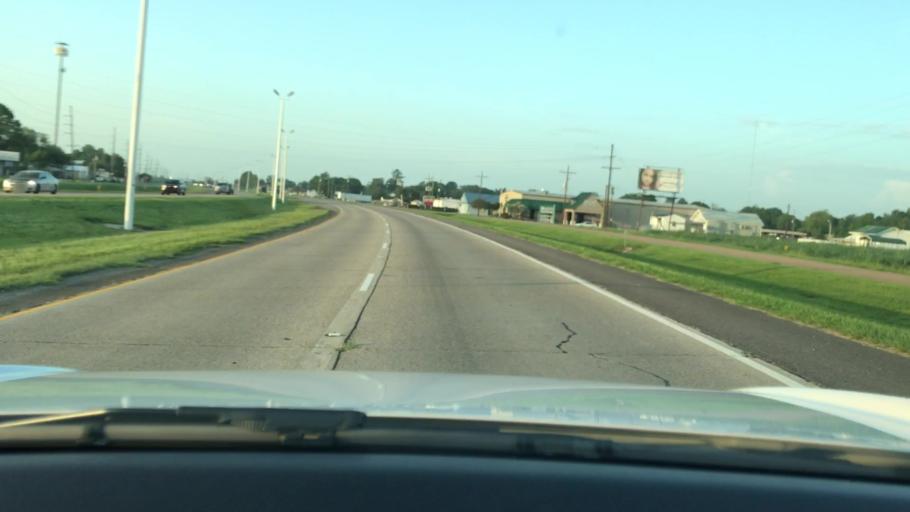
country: US
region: Louisiana
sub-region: West Baton Rouge Parish
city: Addis
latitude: 30.3621
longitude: -91.2612
